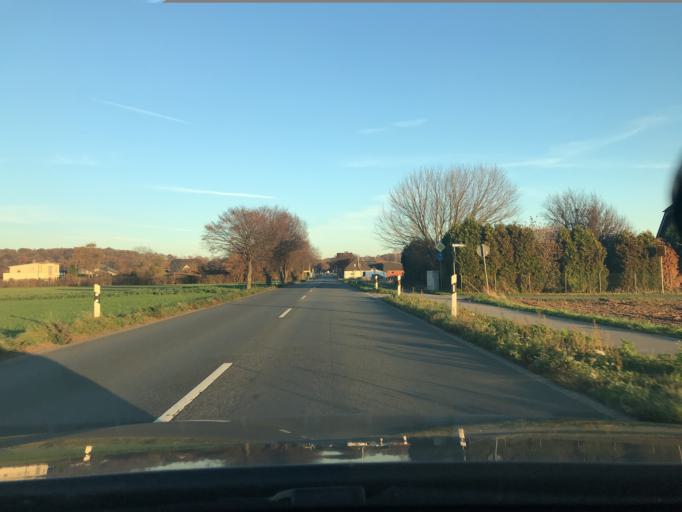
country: DE
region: North Rhine-Westphalia
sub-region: Regierungsbezirk Dusseldorf
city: Rheurdt
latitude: 51.4411
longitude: 6.4561
